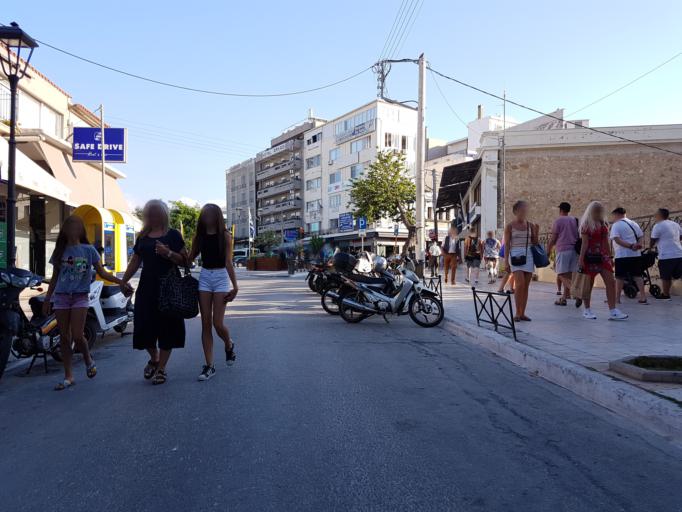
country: GR
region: Crete
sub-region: Nomos Chanias
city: Chania
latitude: 35.5147
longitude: 24.0167
